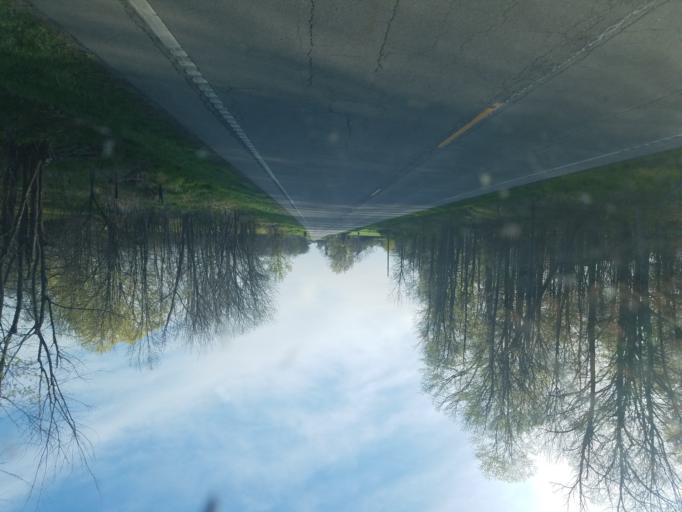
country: US
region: Ohio
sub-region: Huron County
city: New London
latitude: 41.0402
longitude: -82.4277
